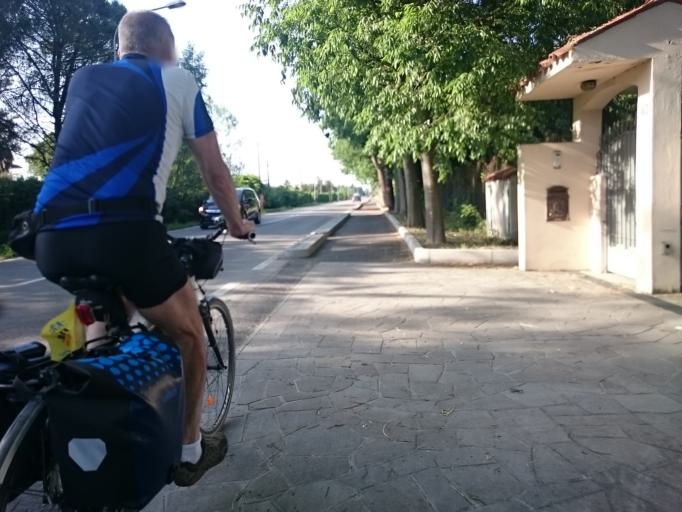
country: IT
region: Veneto
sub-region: Provincia di Padova
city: Mandriola-Sant'Agostino
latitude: 45.3580
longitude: 11.8233
